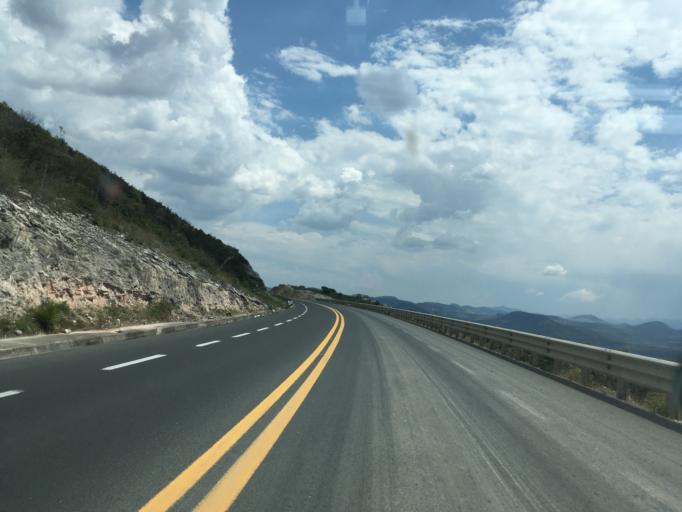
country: MX
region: Puebla
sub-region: San Jose Miahuatlan
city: San Pedro Tetitlan
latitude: 18.0146
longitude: -97.3542
